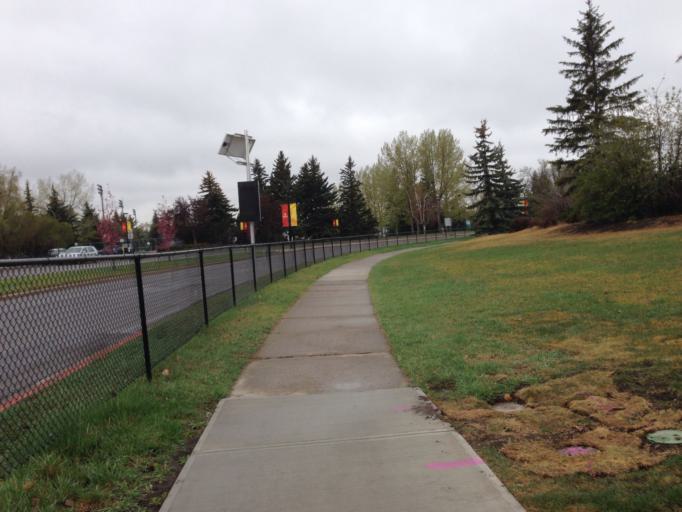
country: CA
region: Alberta
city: Calgary
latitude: 51.0788
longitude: -114.1355
